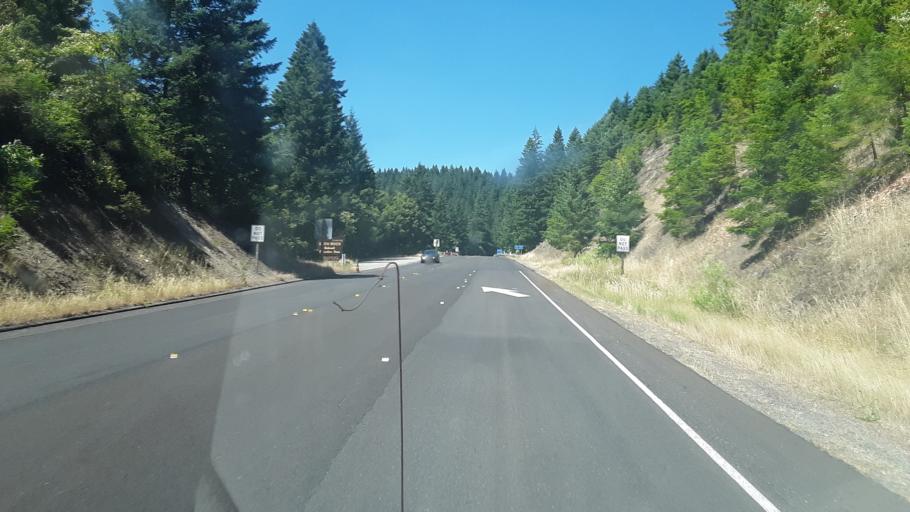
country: US
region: Oregon
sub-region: Josephine County
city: Cave Junction
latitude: 41.9629
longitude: -123.7464
